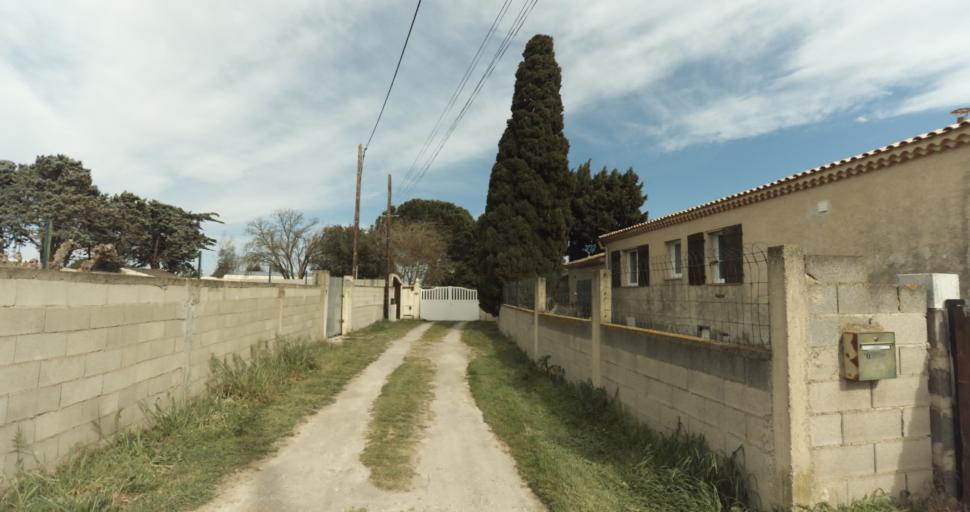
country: FR
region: Languedoc-Roussillon
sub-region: Departement de l'Herault
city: Marseillan
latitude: 43.3338
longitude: 3.5500
